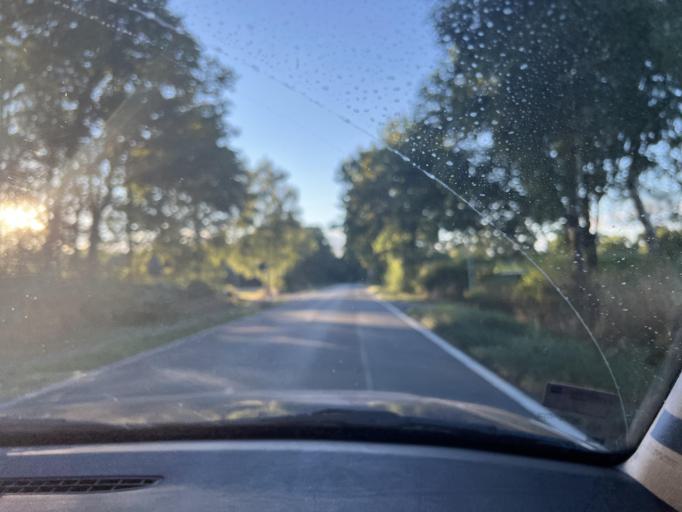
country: DE
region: Schleswig-Holstein
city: Weddingstedt
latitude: 54.2269
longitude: 9.1097
